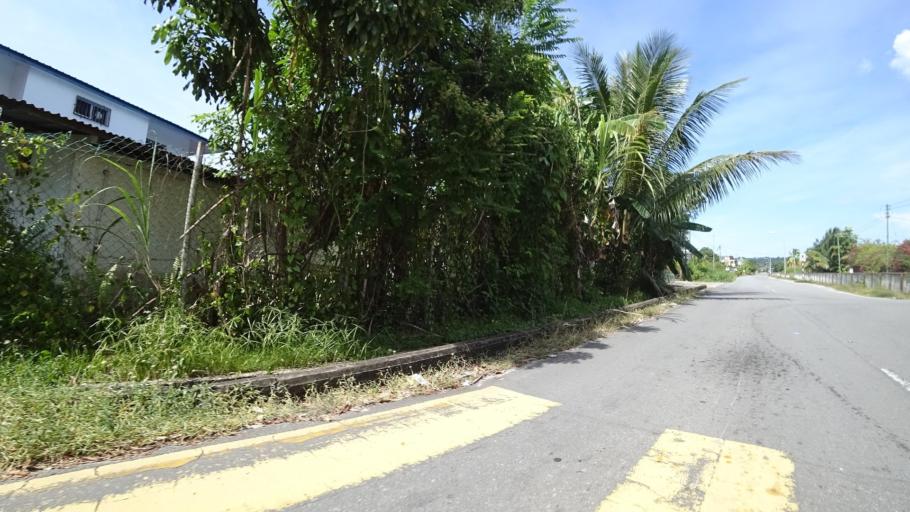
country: BN
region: Brunei and Muara
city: Bandar Seri Begawan
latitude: 4.8874
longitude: 114.8458
